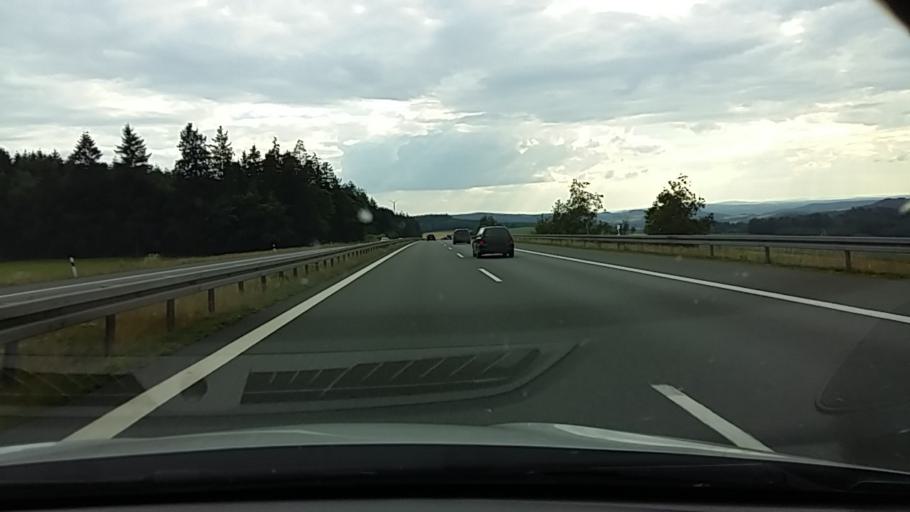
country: DE
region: Bavaria
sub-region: Upper Palatinate
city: Leuchtenberg
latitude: 49.5918
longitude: 12.2985
